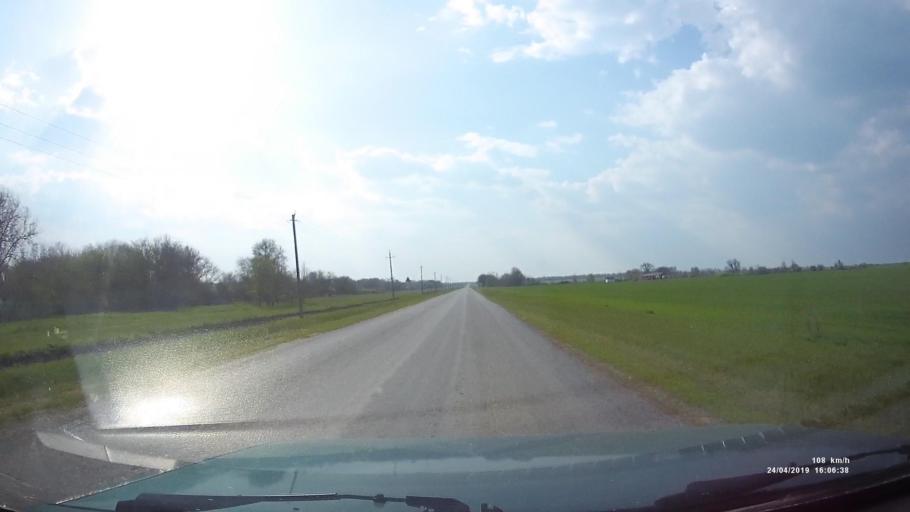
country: RU
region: Rostov
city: Sovetskoye
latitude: 46.6884
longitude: 42.3431
